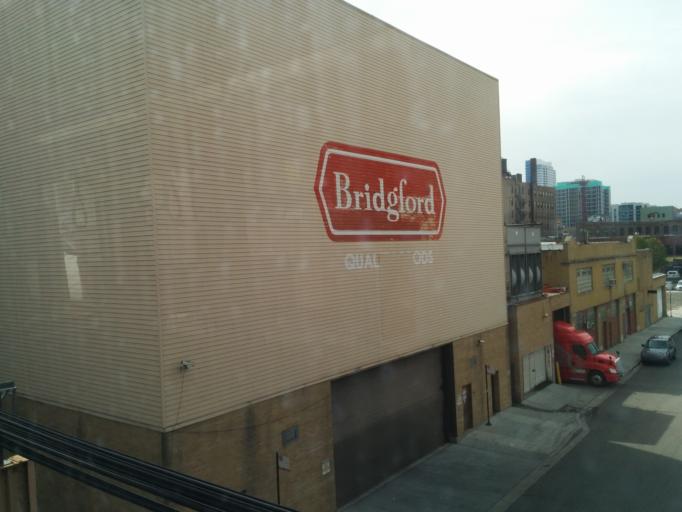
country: US
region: Illinois
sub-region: Cook County
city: Chicago
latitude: 41.8856
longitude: -87.6498
